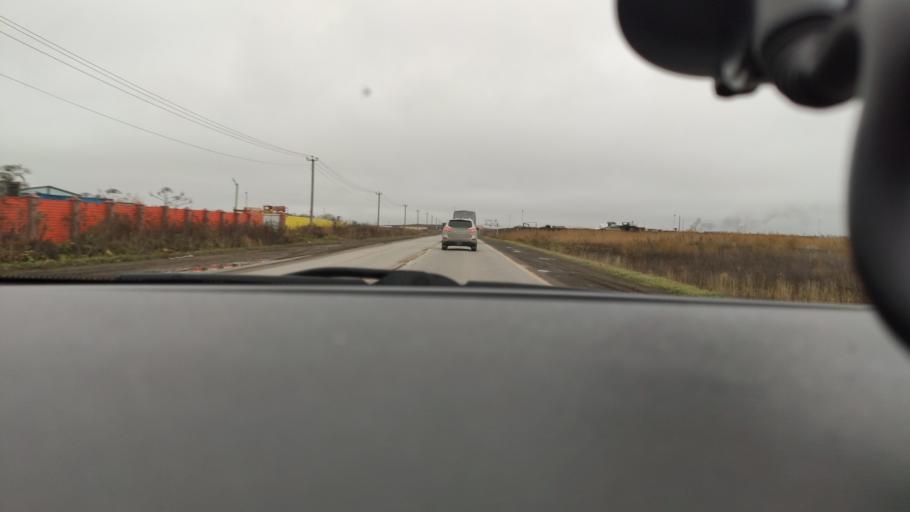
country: RU
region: Perm
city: Froly
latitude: 57.9153
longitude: 56.1865
